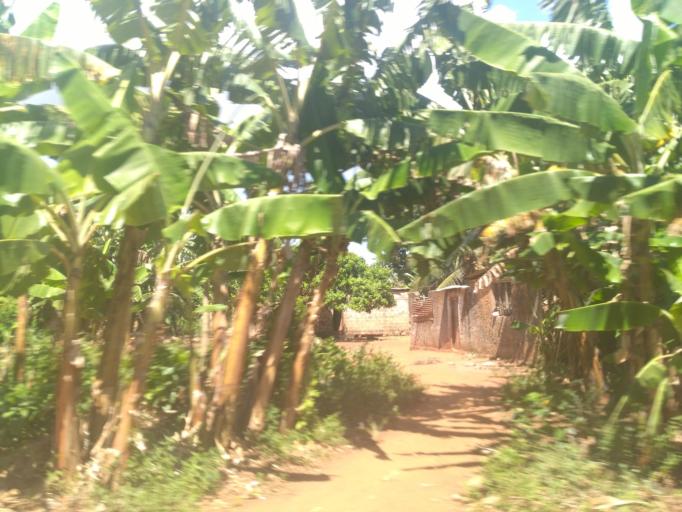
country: TZ
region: Zanzibar North
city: Gamba
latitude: -5.9374
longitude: 39.3404
